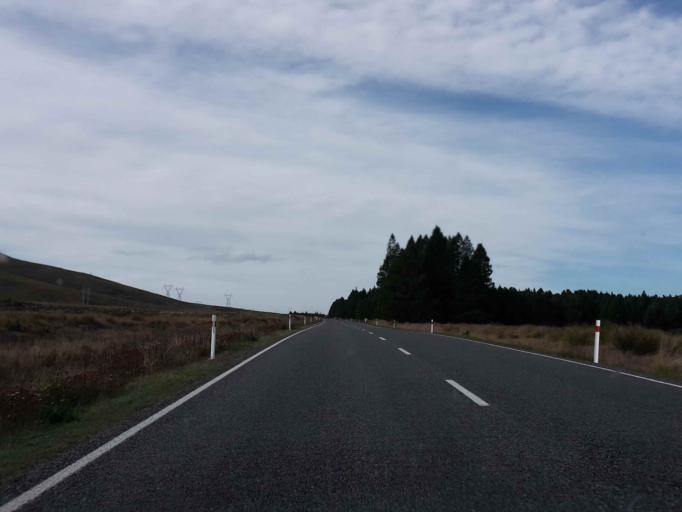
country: NZ
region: Canterbury
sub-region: Timaru District
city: Pleasant Point
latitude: -44.0913
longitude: 170.5845
